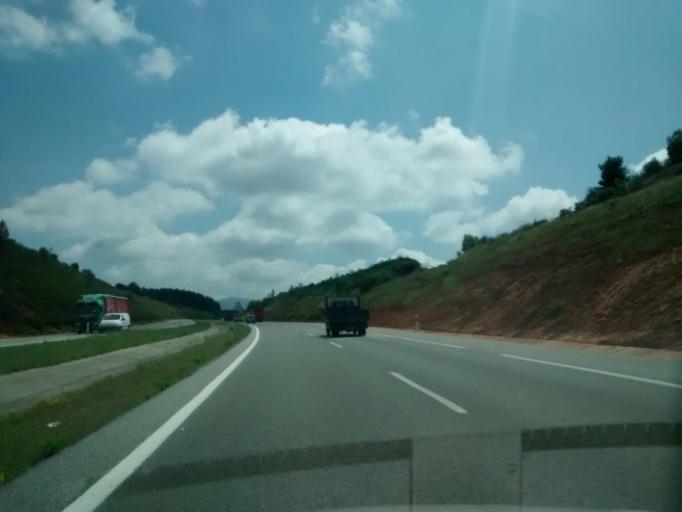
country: ES
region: Castille and Leon
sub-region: Provincia de Leon
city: Ponferrada
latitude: 42.5683
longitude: -6.5904
